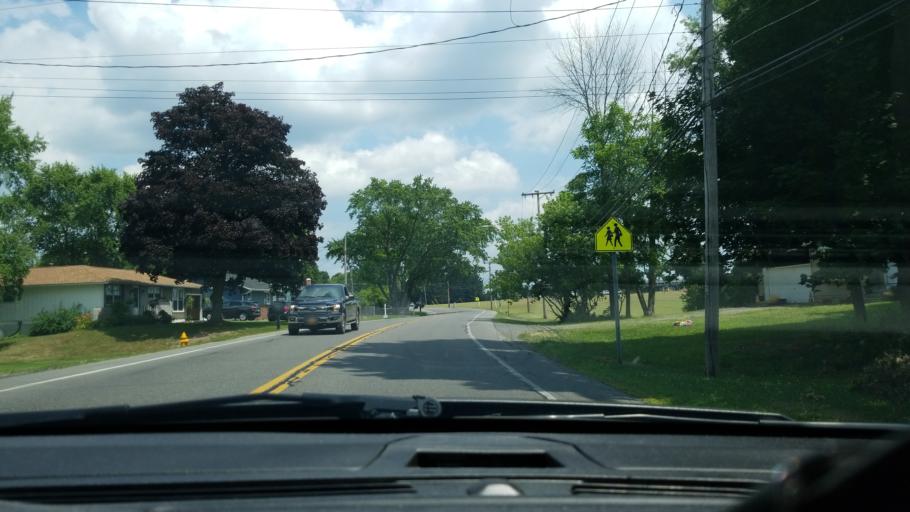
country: US
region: New York
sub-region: Onondaga County
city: Liverpool
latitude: 43.1500
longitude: -76.2233
